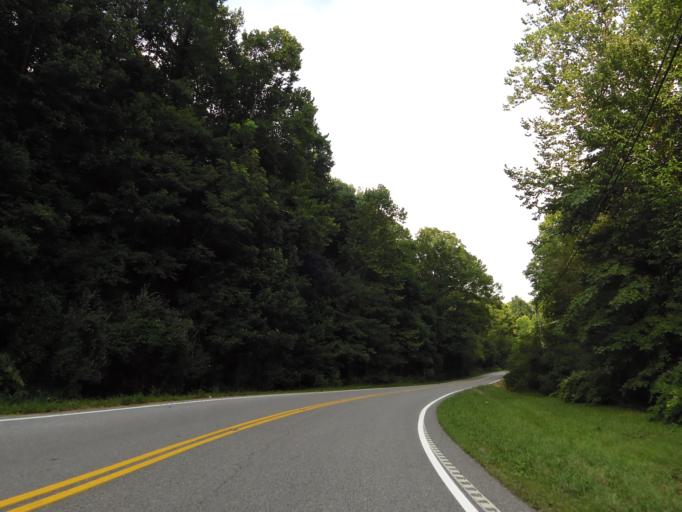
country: US
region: Tennessee
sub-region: Morgan County
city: Coalfield
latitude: 36.1254
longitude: -84.4223
